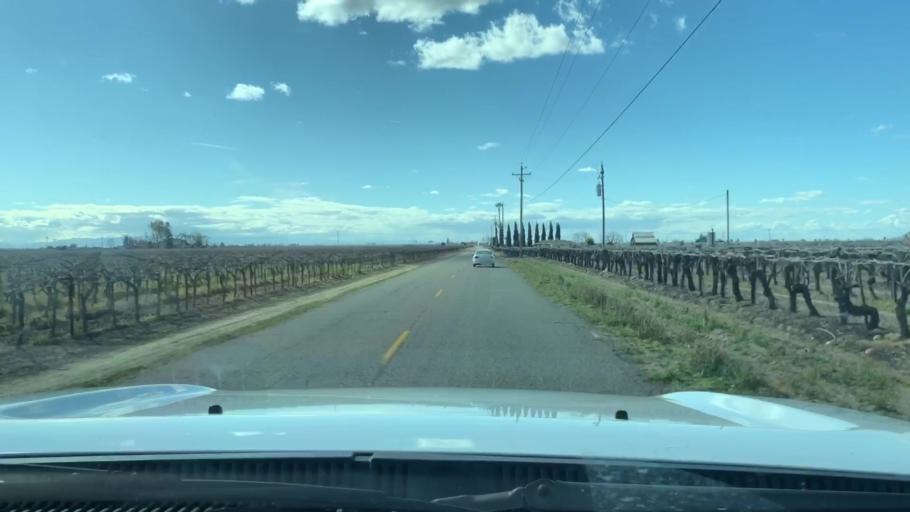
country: US
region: California
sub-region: Fresno County
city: Caruthers
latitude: 36.5619
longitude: -119.7675
